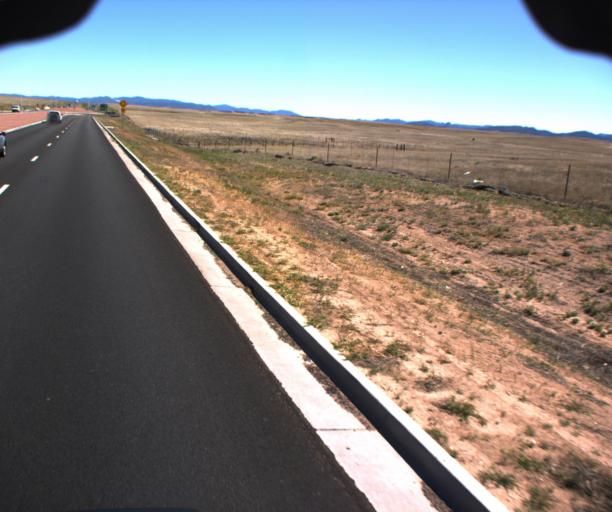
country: US
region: Arizona
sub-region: Yavapai County
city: Chino Valley
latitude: 34.7091
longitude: -112.4518
